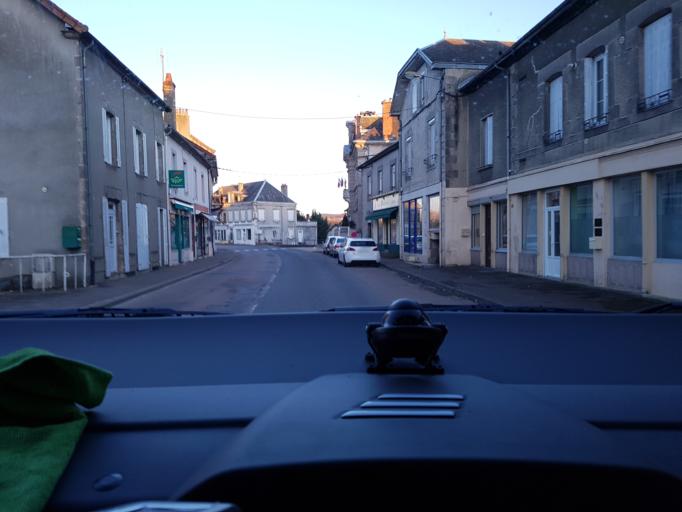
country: FR
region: Bourgogne
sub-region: Departement de Saone-et-Loire
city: Etang-sur-Arroux
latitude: 46.8669
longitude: 4.1837
